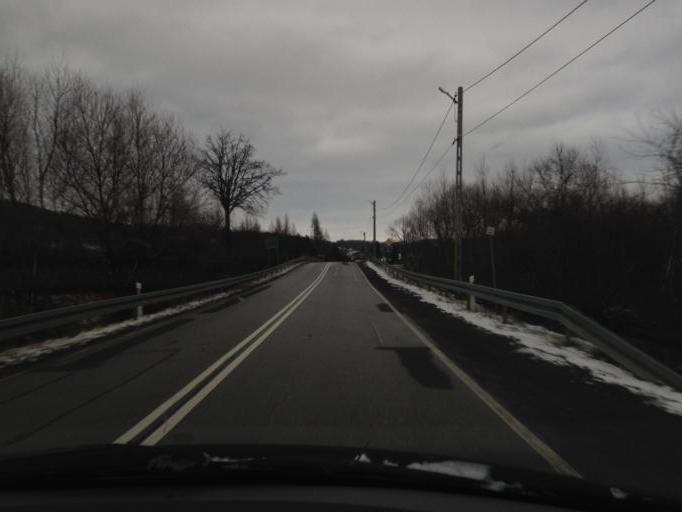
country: PL
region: Lesser Poland Voivodeship
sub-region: Powiat tarnowski
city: Gromnik
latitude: 49.8401
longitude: 20.9797
